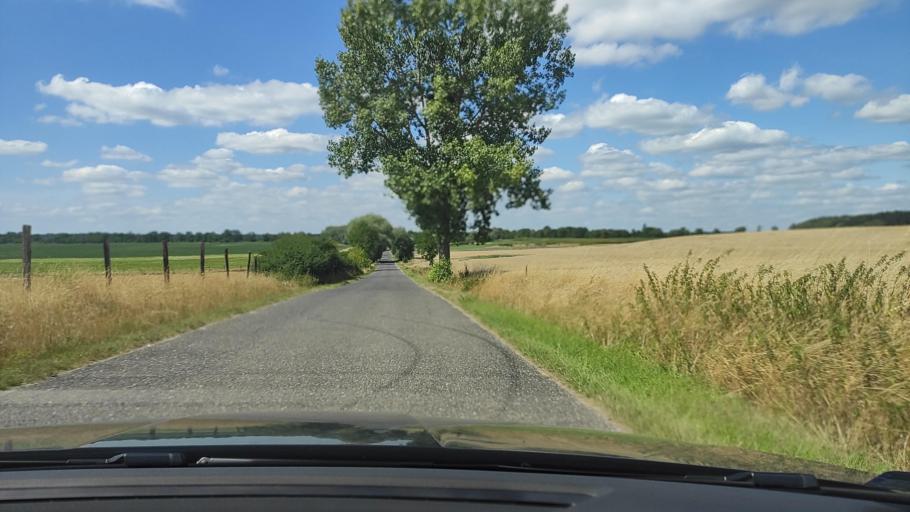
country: PL
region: Greater Poland Voivodeship
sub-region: Powiat poznanski
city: Kobylnica
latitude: 52.4899
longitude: 17.1329
